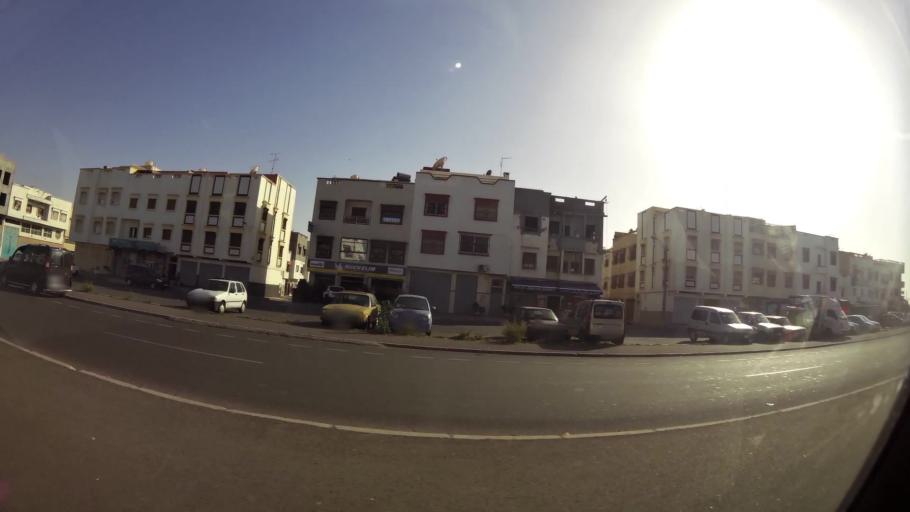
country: MA
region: Oued ed Dahab-Lagouira
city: Dakhla
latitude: 30.3942
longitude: -9.5339
